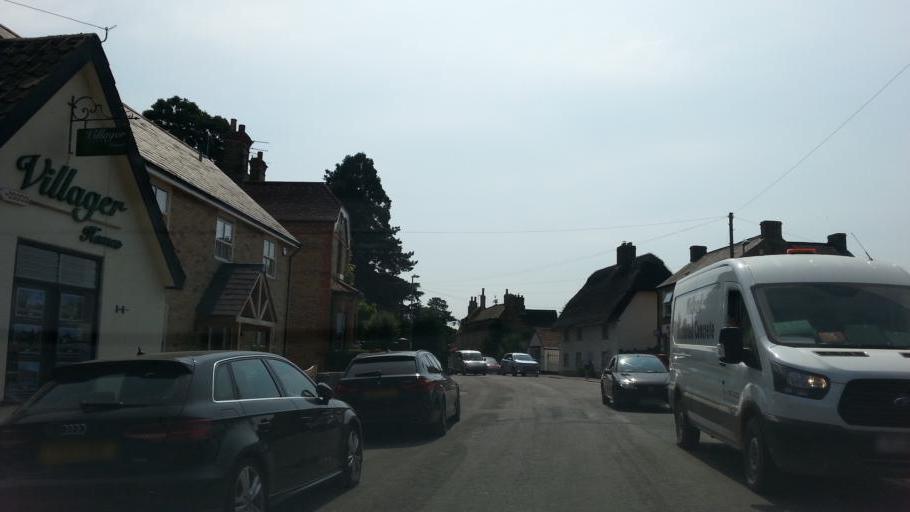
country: GB
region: England
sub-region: Cambridgeshire
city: Brampton
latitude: 52.3220
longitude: -0.2243
